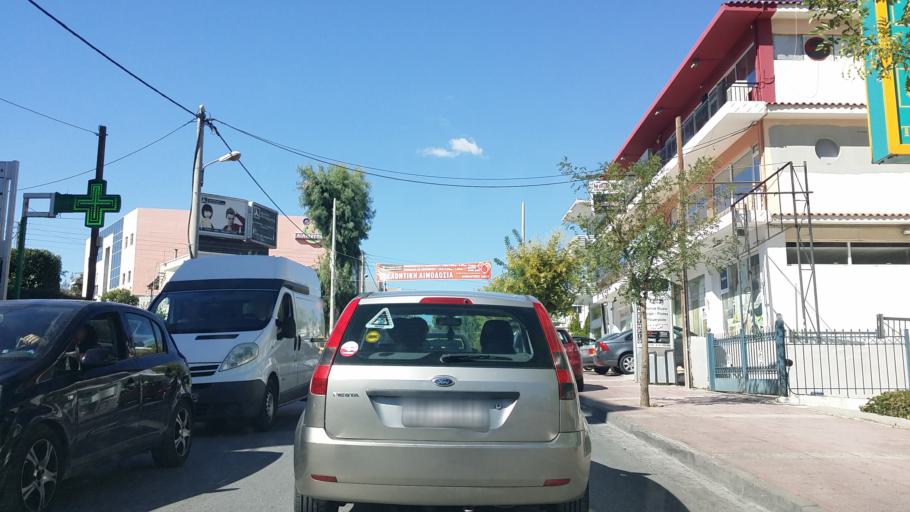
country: GR
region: Attica
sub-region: Nomarchia Athinas
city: Ilion
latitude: 38.0313
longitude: 23.7117
